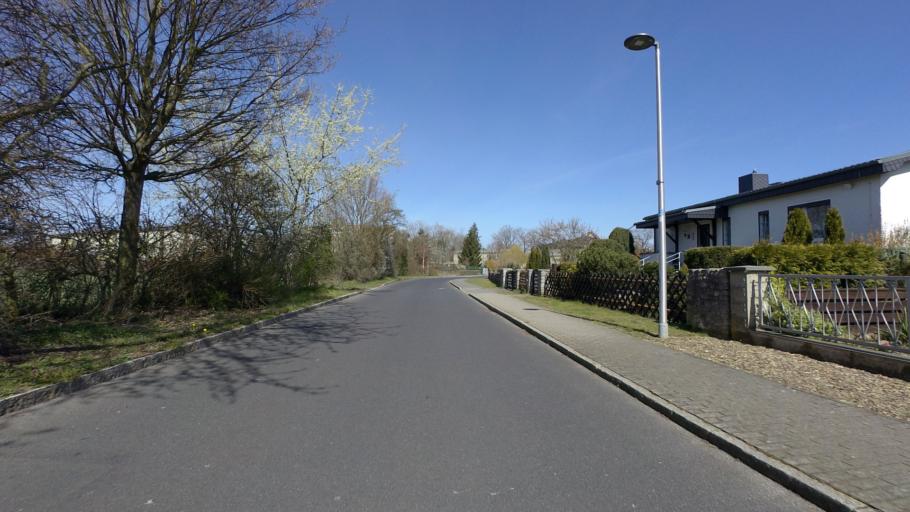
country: DE
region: Brandenburg
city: Rangsdorf
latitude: 52.3238
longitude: 13.4272
